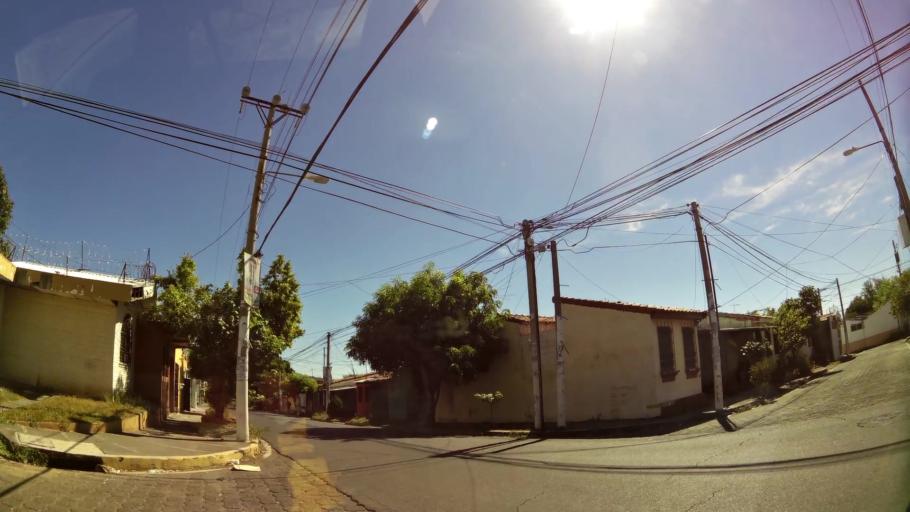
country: SV
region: San Miguel
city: San Miguel
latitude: 13.4922
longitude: -88.1683
